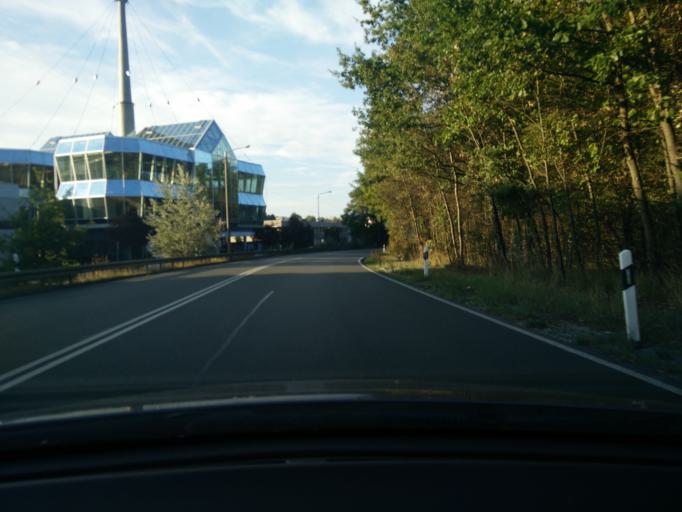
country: DE
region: Bavaria
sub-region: Regierungsbezirk Mittelfranken
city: Wendelstein
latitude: 49.4024
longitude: 11.1280
